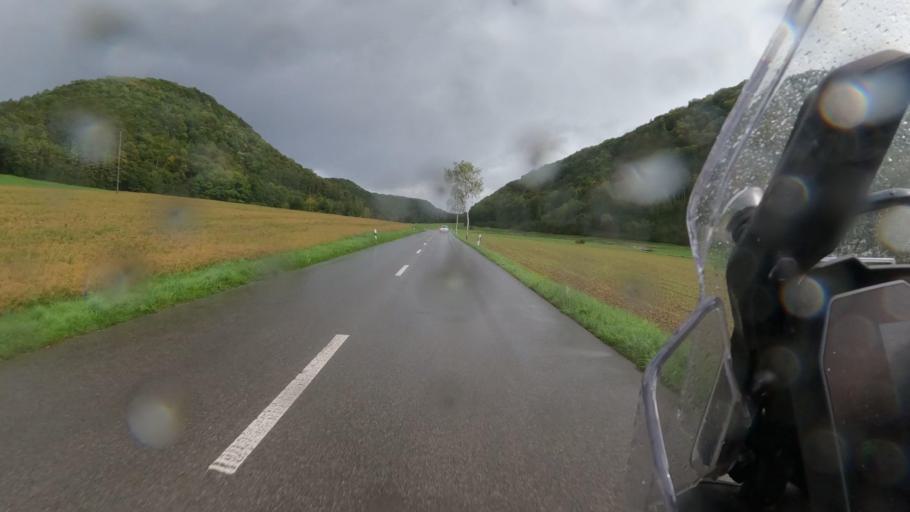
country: CH
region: Schaffhausen
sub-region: Bezirk Unterklettgau
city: Wilchingen
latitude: 47.6499
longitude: 8.4987
